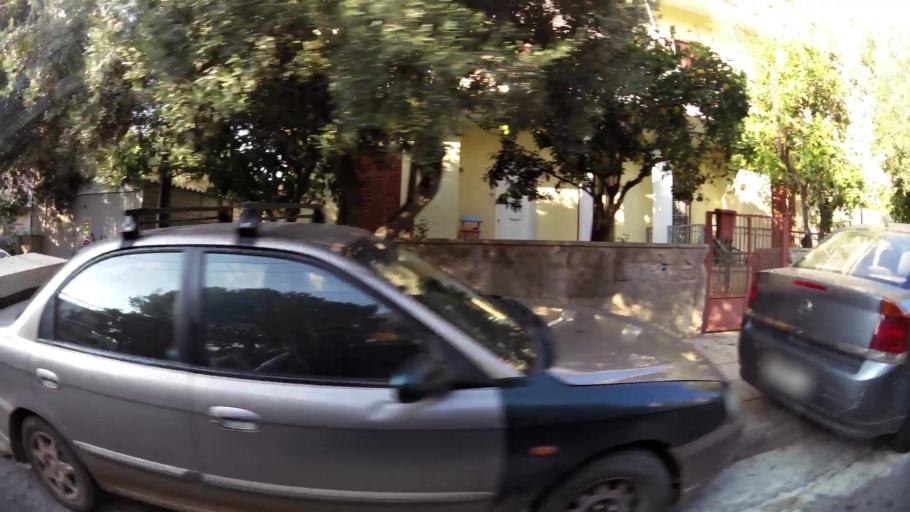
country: GR
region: Attica
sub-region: Nomarchia Athinas
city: Argyroupoli
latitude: 37.8951
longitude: 23.7512
